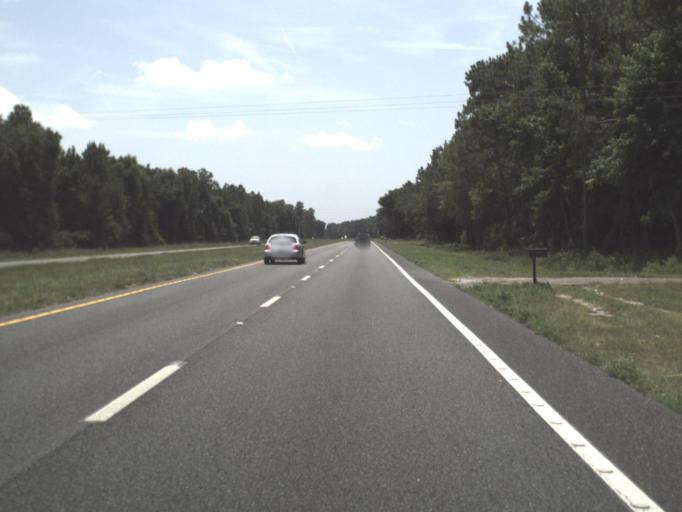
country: US
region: Florida
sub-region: Taylor County
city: Perry
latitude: 29.9916
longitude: -83.4993
